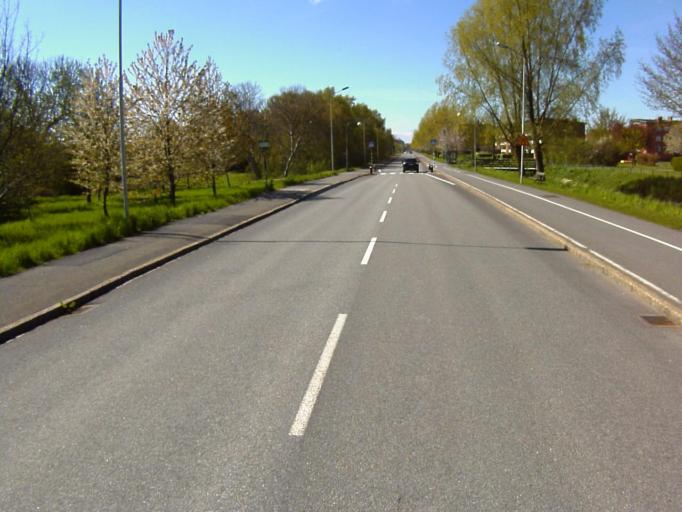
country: SE
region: Skane
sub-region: Kristianstads Kommun
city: Kristianstad
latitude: 56.0474
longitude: 14.1680
